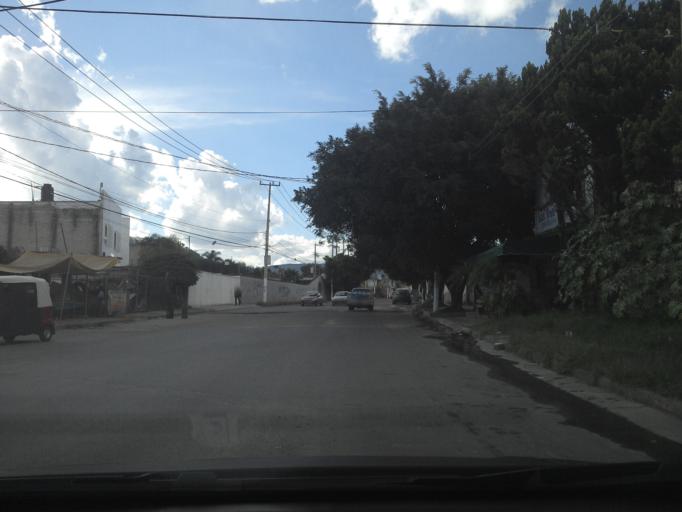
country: MX
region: Jalisco
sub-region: Tlajomulco de Zuniga
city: Palomar
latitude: 20.6179
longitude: -103.4515
